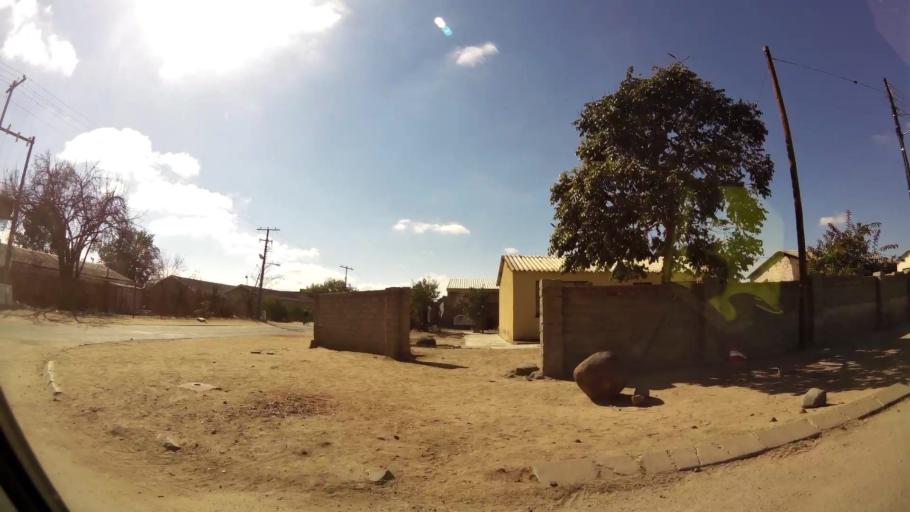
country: ZA
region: Limpopo
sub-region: Capricorn District Municipality
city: Polokwane
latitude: -23.8603
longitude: 29.3894
